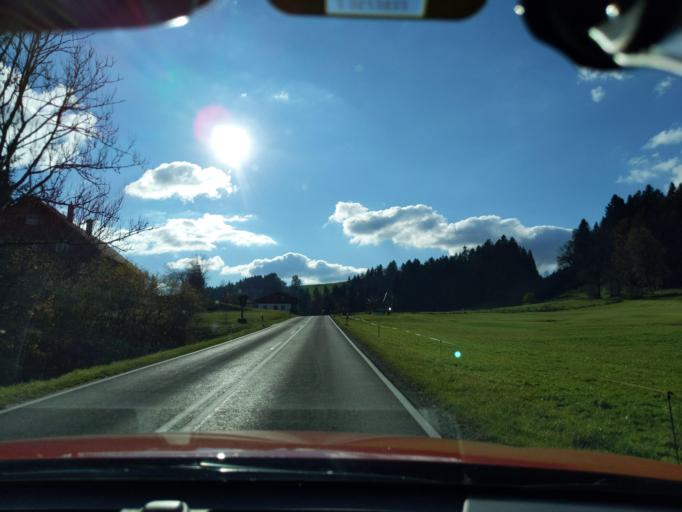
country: DE
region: Bavaria
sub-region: Swabia
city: Weiler-Simmerberg
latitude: 47.5750
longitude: 9.8931
